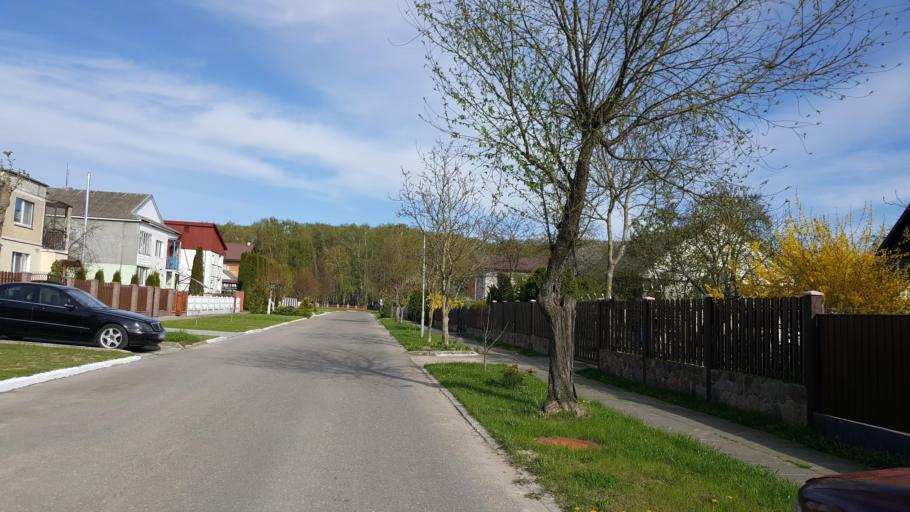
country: BY
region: Brest
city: Vysokaye
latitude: 52.4013
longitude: 23.4574
